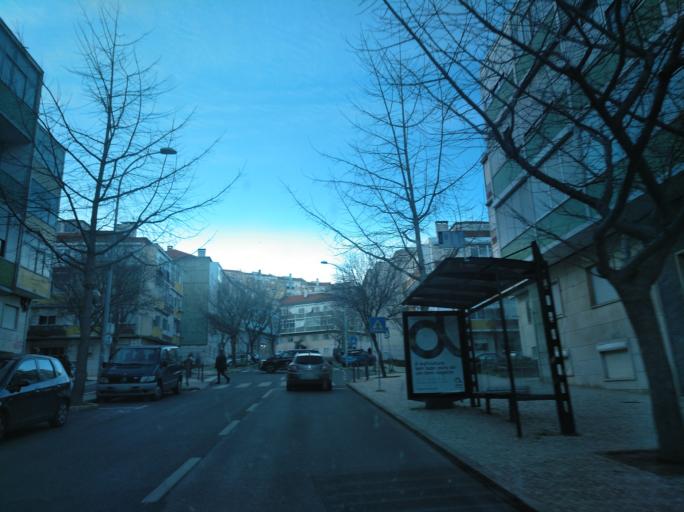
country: PT
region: Lisbon
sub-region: Amadora
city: Amadora
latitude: 38.7452
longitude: -9.2219
